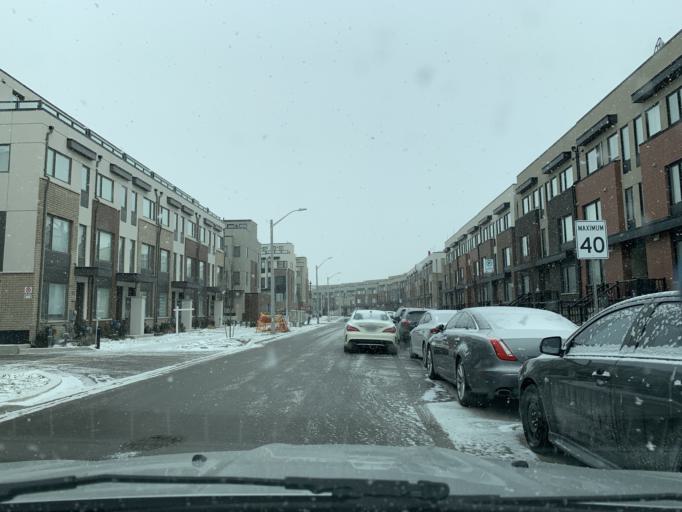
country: CA
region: Ontario
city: Concord
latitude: 43.7359
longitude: -79.4760
